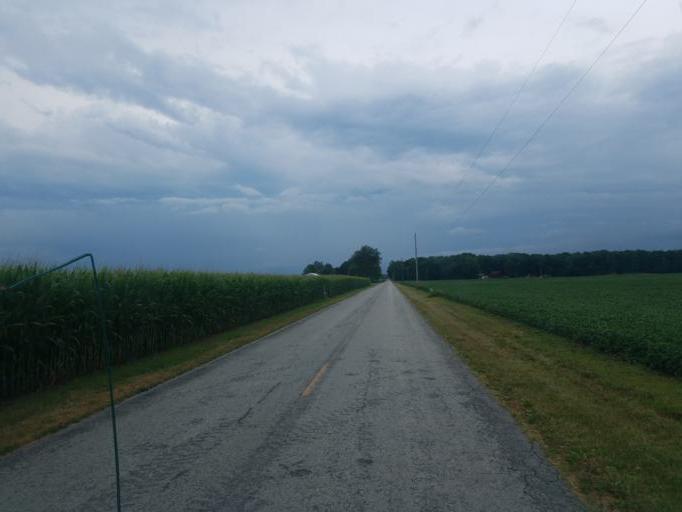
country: US
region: Ohio
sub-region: Defiance County
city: Hicksville
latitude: 41.2373
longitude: -84.7616
